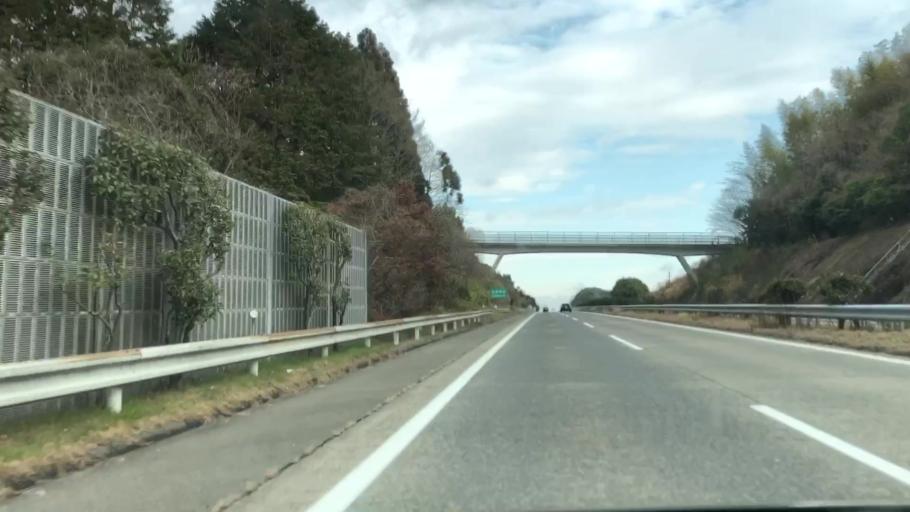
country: JP
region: Saga Prefecture
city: Kanzakimachi-kanzaki
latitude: 33.3570
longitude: 130.4234
